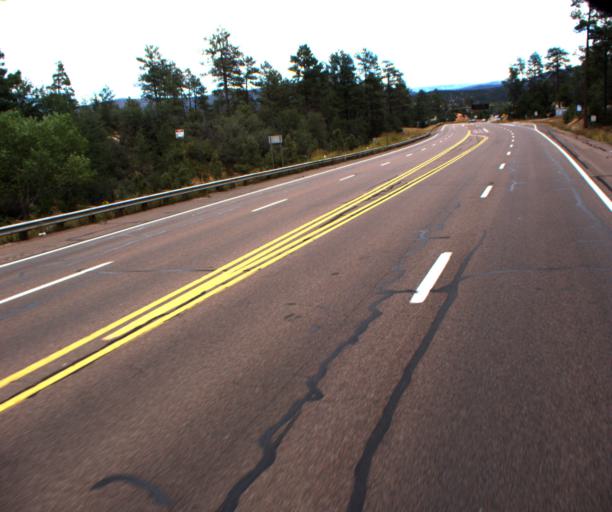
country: US
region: Arizona
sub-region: Gila County
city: Sun Valley
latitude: 34.2518
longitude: -111.2739
